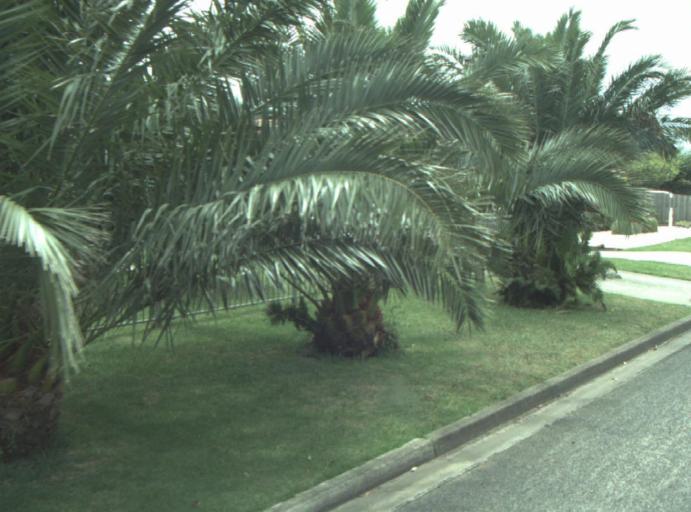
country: AU
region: Victoria
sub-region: Queenscliffe
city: Queenscliff
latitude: -38.1357
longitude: 144.7037
